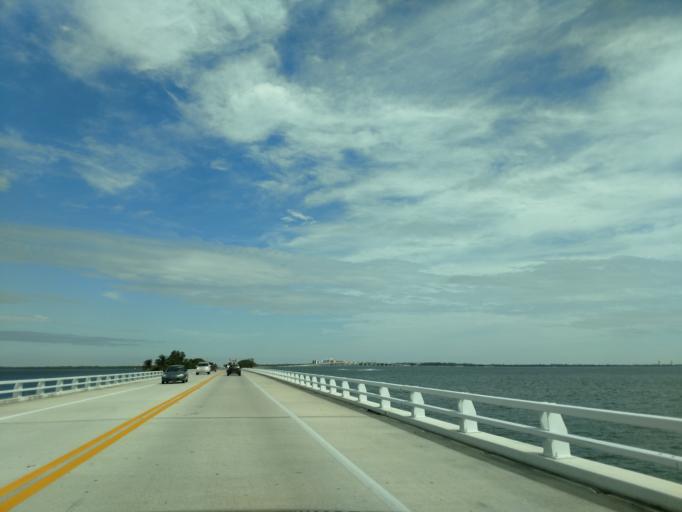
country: US
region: Florida
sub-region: Lee County
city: Sanibel
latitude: 26.4611
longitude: -82.0326
